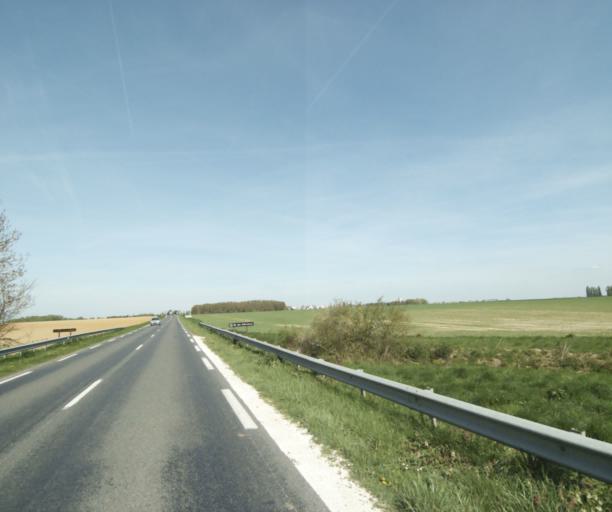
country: FR
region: Ile-de-France
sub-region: Departement de Seine-et-Marne
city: Nangis
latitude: 48.5367
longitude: 3.0212
